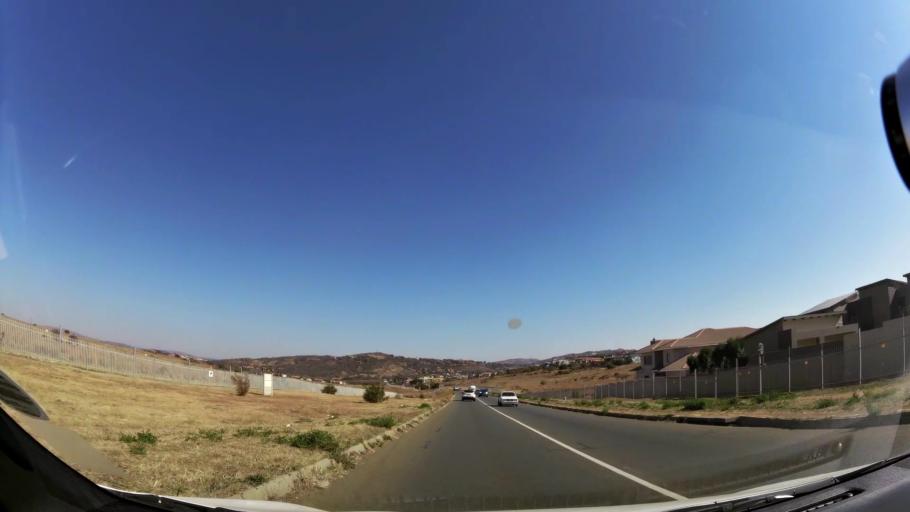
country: ZA
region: Gauteng
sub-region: City of Johannesburg Metropolitan Municipality
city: Johannesburg
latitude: -26.2905
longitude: 28.0836
